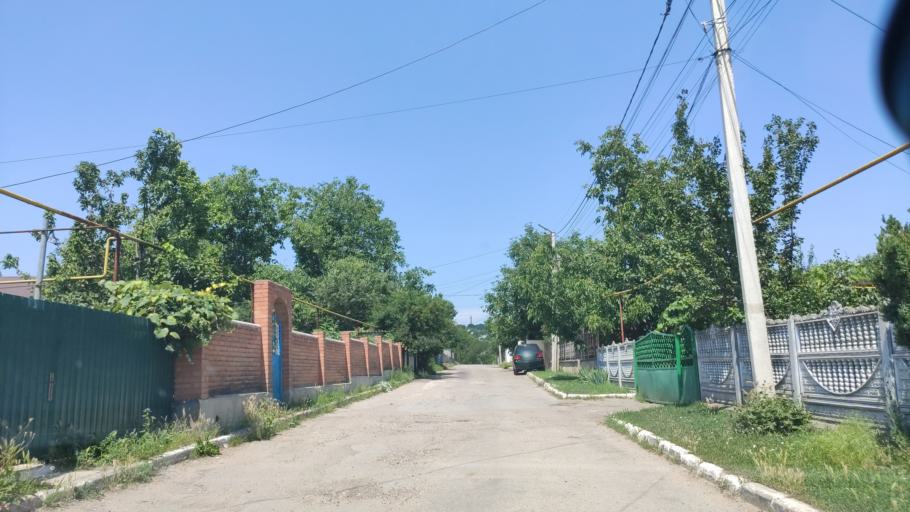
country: MD
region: Raionul Soroca
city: Soroca
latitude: 48.1674
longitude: 28.3082
